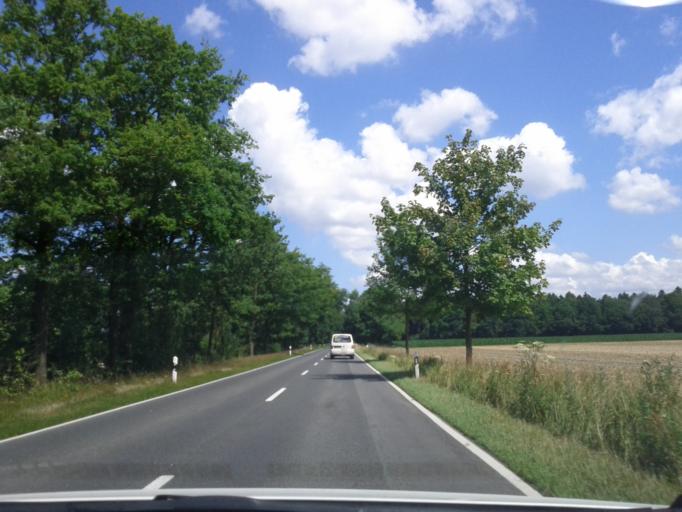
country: DE
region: Lower Saxony
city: Lengenbostel
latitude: 53.3234
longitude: 9.5240
